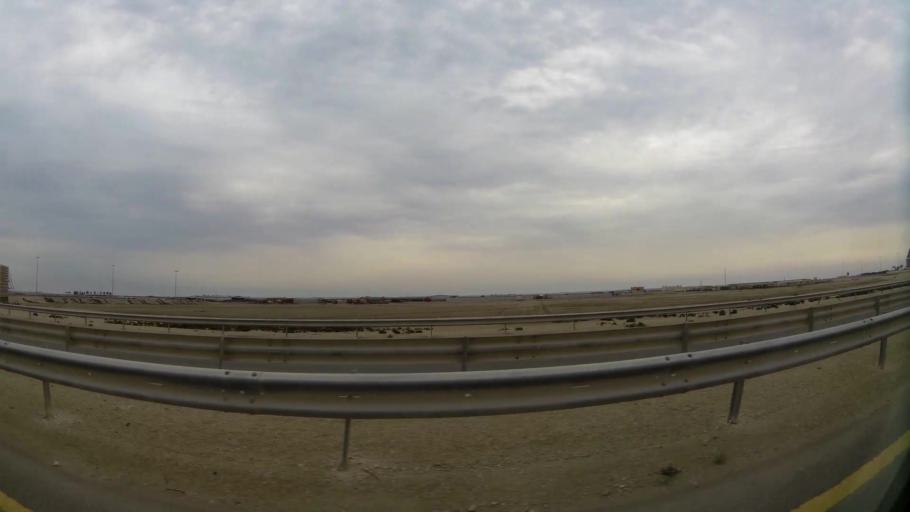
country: BH
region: Central Governorate
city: Dar Kulayb
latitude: 25.8437
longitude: 50.5844
